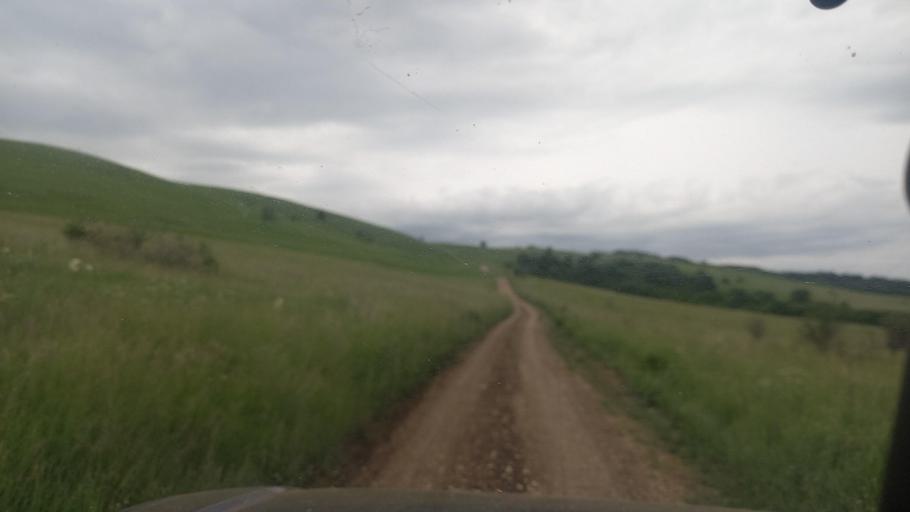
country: RU
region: Krasnodarskiy
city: Peredovaya
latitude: 44.0788
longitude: 41.3642
